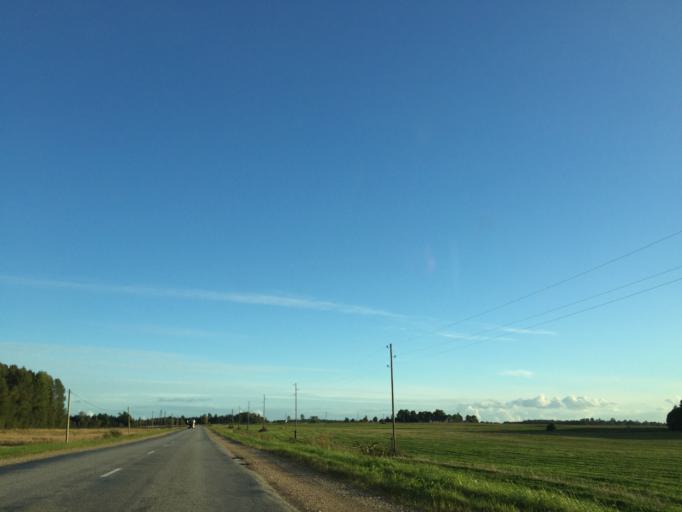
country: LV
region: Saldus Rajons
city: Saldus
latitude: 56.7423
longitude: 22.3775
